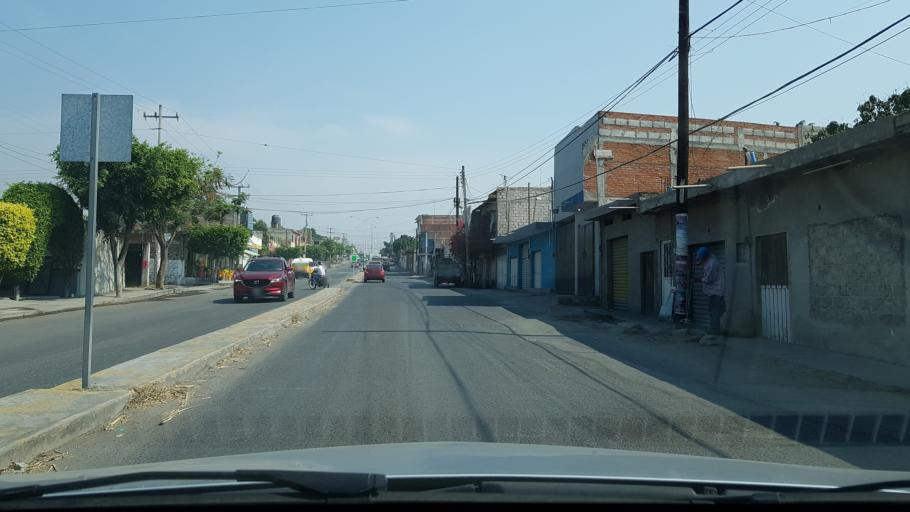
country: MX
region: Morelos
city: Zacatepec
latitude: 18.6695
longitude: -99.1856
